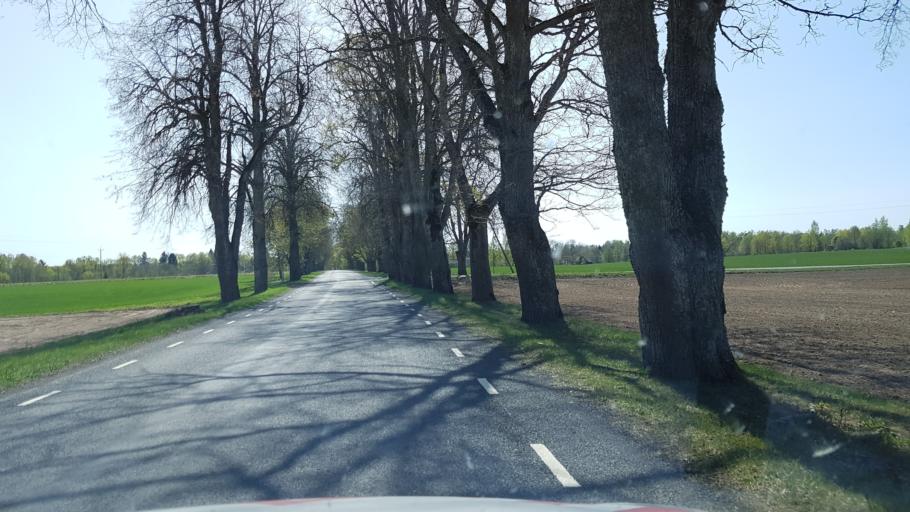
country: EE
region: Viljandimaa
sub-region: Vohma linn
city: Vohma
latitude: 58.5355
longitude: 25.5825
